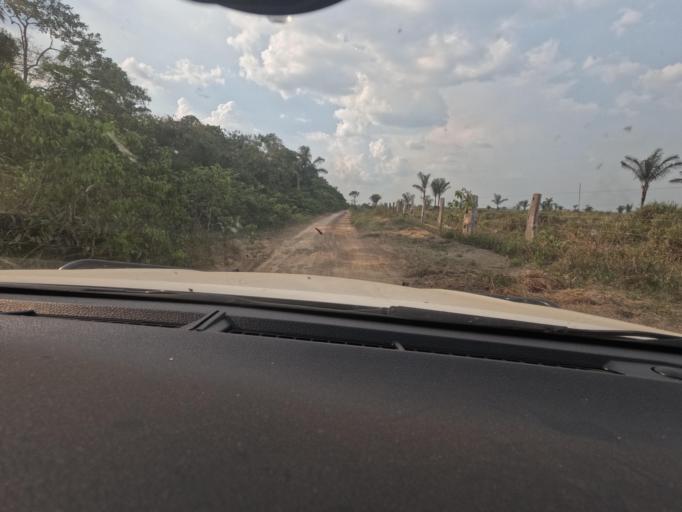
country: BR
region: Rondonia
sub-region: Porto Velho
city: Porto Velho
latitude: -8.6427
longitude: -63.1556
